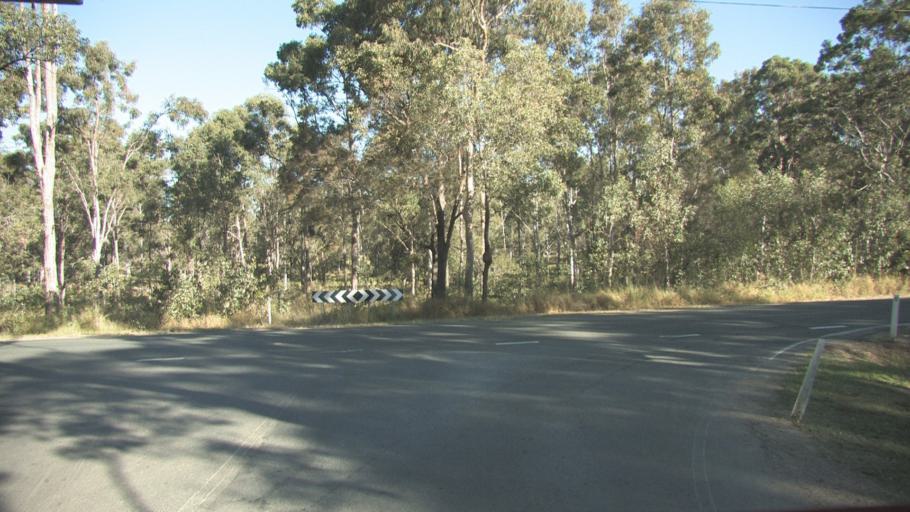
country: AU
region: Queensland
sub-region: Logan
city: North Maclean
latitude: -27.7560
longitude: 153.0132
